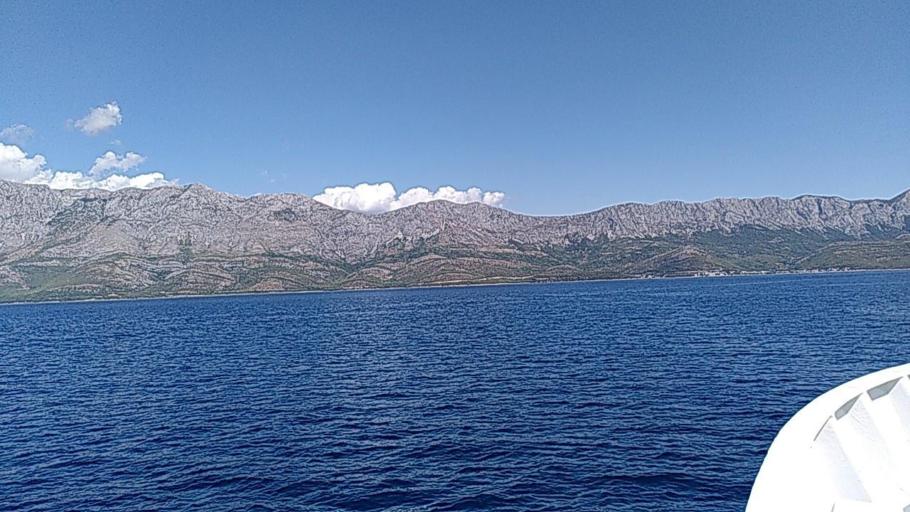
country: HR
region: Dubrovacko-Neretvanska
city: Orebic
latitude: 43.1255
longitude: 17.2009
